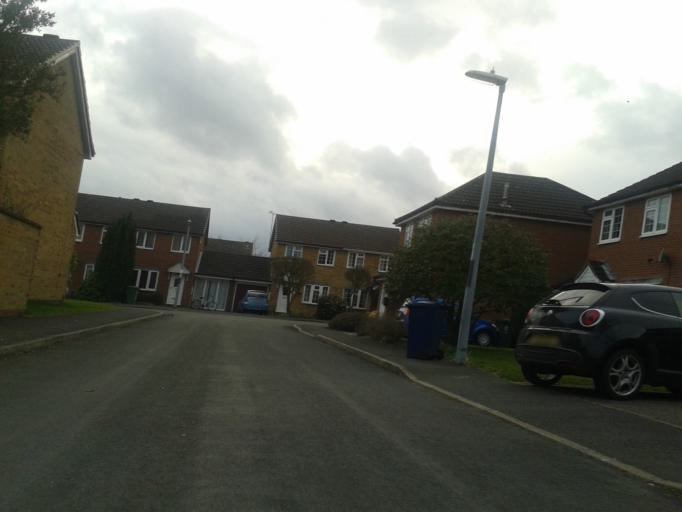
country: GB
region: England
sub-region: Cambridgeshire
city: Fulbourn
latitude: 52.1944
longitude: 0.1865
